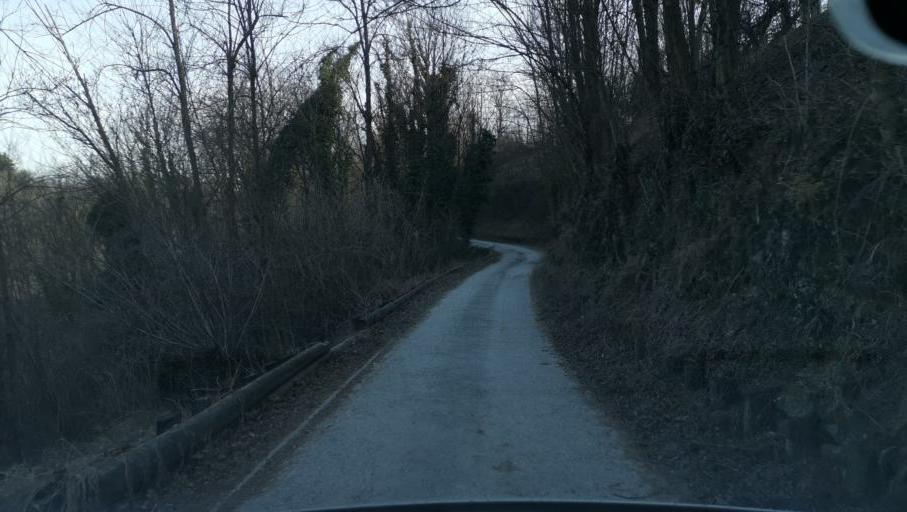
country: IT
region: Piedmont
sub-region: Provincia di Torino
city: Gassino Torinese
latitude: 45.1142
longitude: 7.8274
